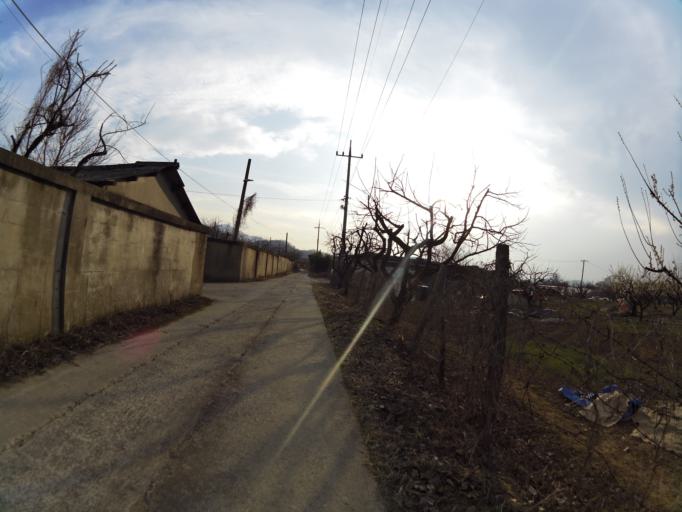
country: KR
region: Gyeongsangbuk-do
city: Gyeongsan-si
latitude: 35.8567
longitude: 128.7154
